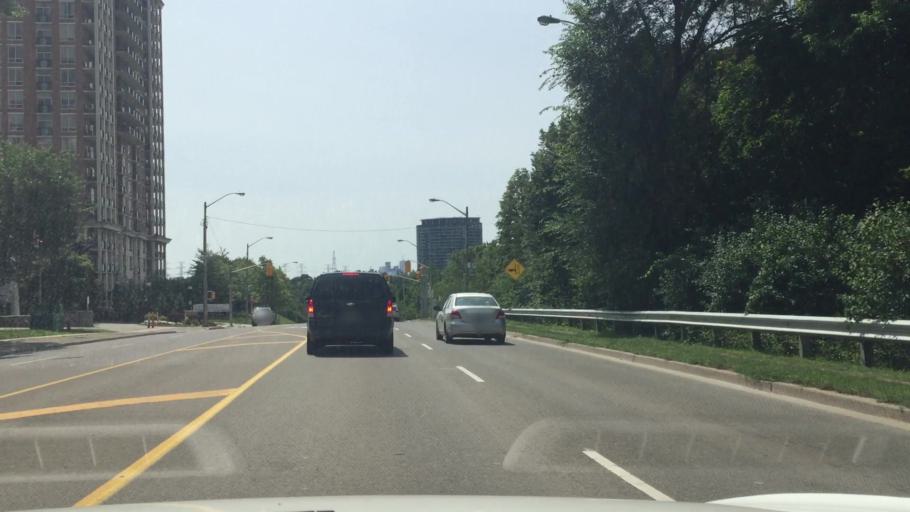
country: CA
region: Ontario
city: Willowdale
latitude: 43.7218
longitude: -79.3494
